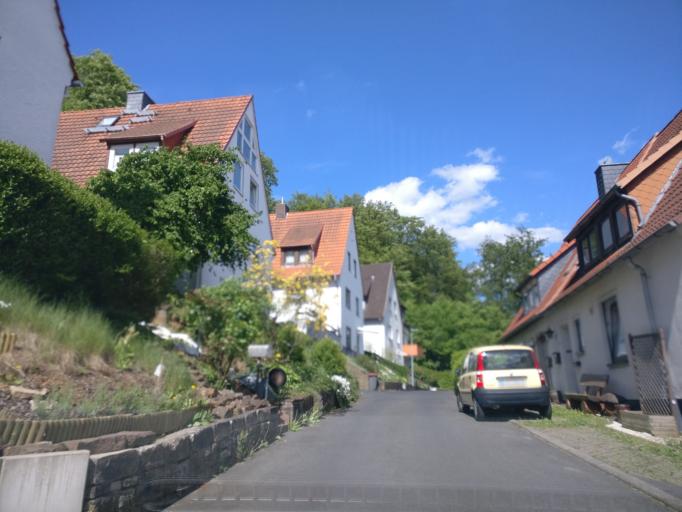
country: DE
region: Lower Saxony
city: Hannoversch Munden
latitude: 51.4144
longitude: 9.6415
